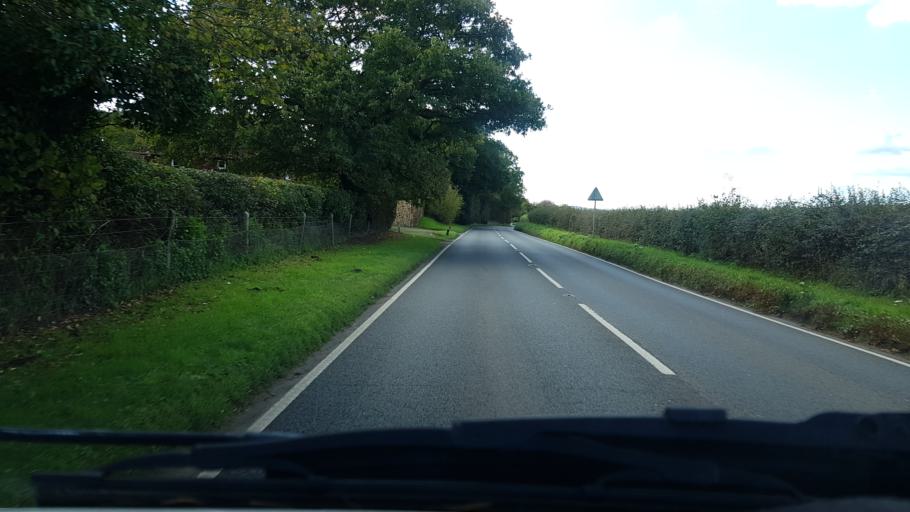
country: GB
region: England
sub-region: Surrey
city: East Horsley
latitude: 51.2147
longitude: -0.4013
